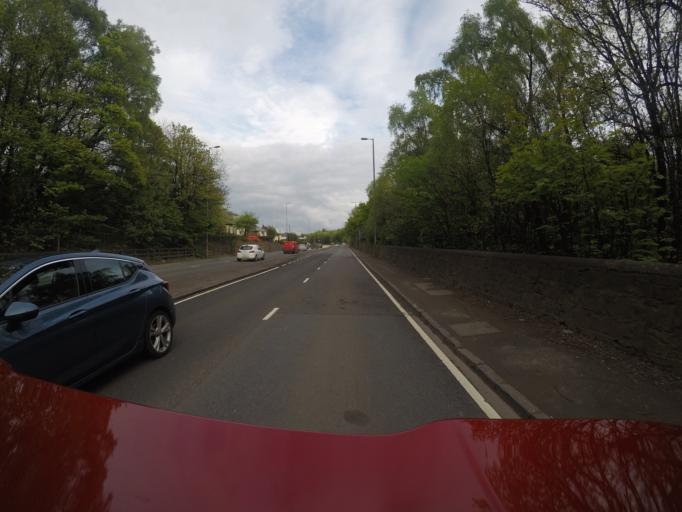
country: GB
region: Scotland
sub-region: Renfrewshire
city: Bishopton
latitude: 55.9359
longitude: -4.5297
